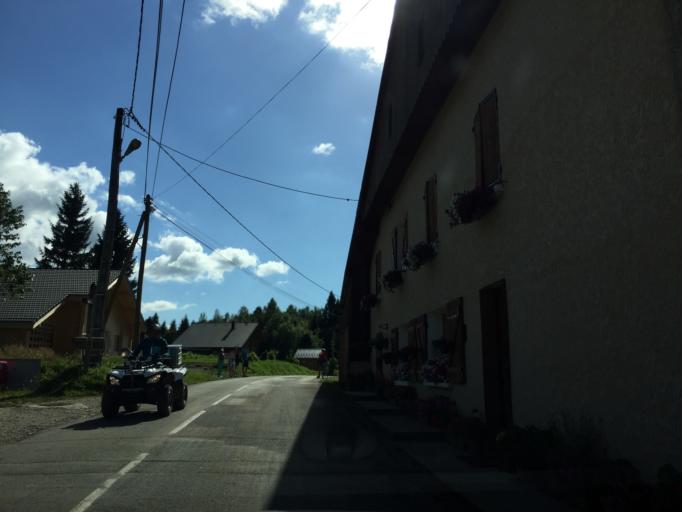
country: FR
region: Rhone-Alpes
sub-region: Departement de la Savoie
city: Coise-Saint-Jean-Pied-Gauthier
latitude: 45.4860
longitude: 6.1984
